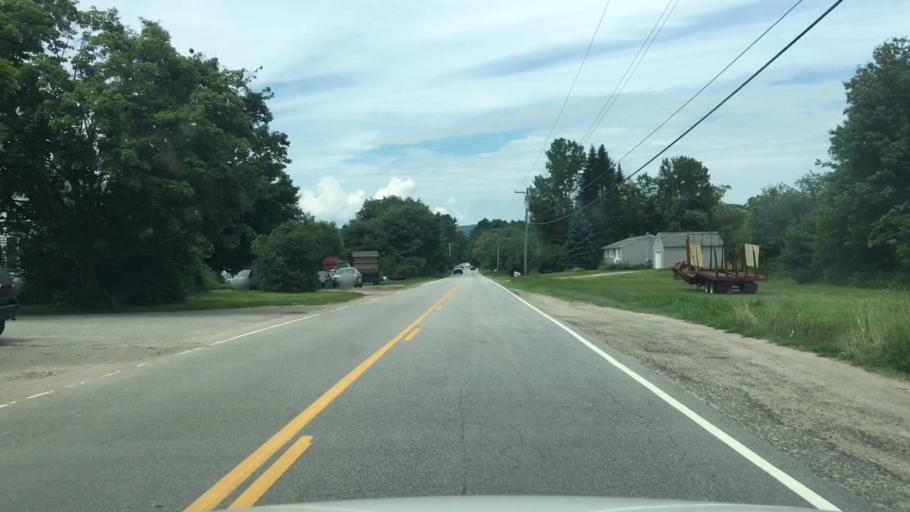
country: US
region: New Hampshire
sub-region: Grafton County
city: Rumney
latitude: 43.7801
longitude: -71.7589
